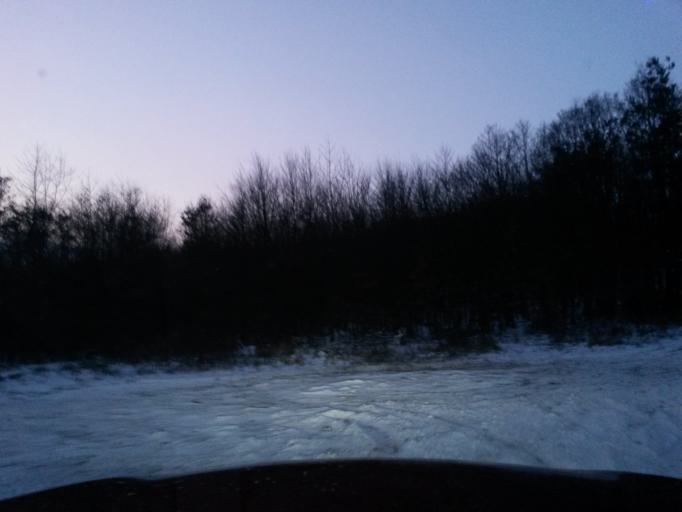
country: SK
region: Kosicky
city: Kosice
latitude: 48.7413
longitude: 21.3168
